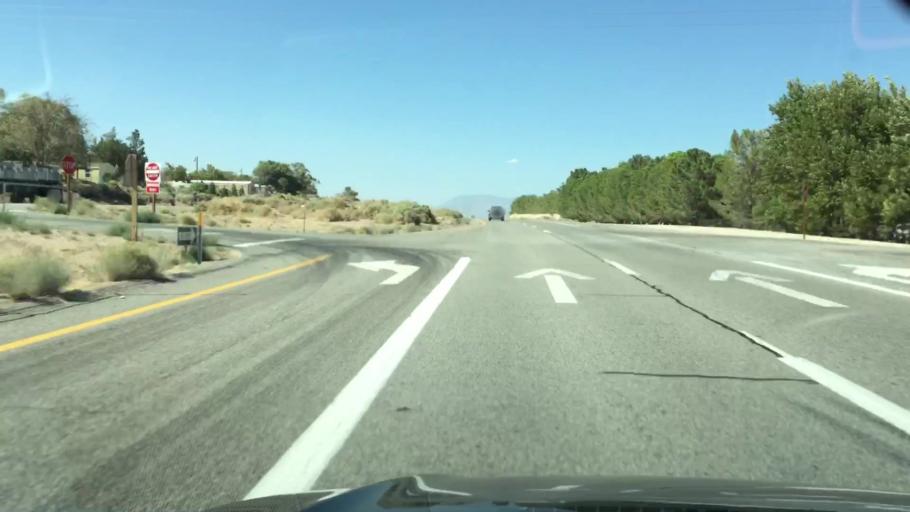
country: US
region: California
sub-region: Inyo County
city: Lone Pine
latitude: 36.5428
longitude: -118.0471
